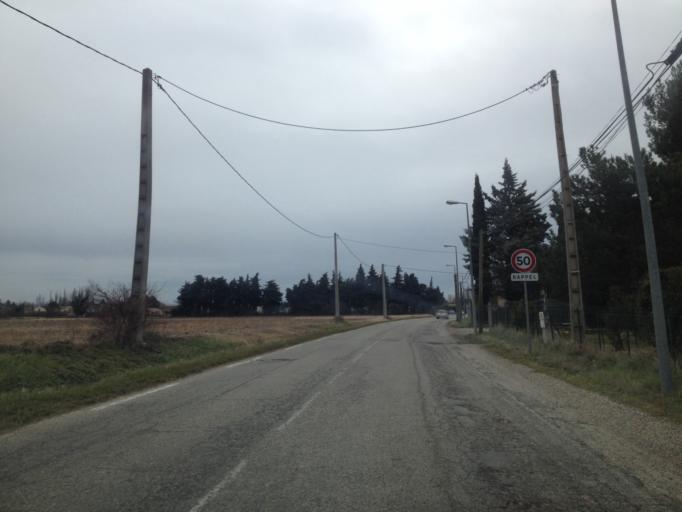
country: FR
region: Provence-Alpes-Cote d'Azur
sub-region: Departement du Vaucluse
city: Jonquieres
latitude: 44.1235
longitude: 4.8989
